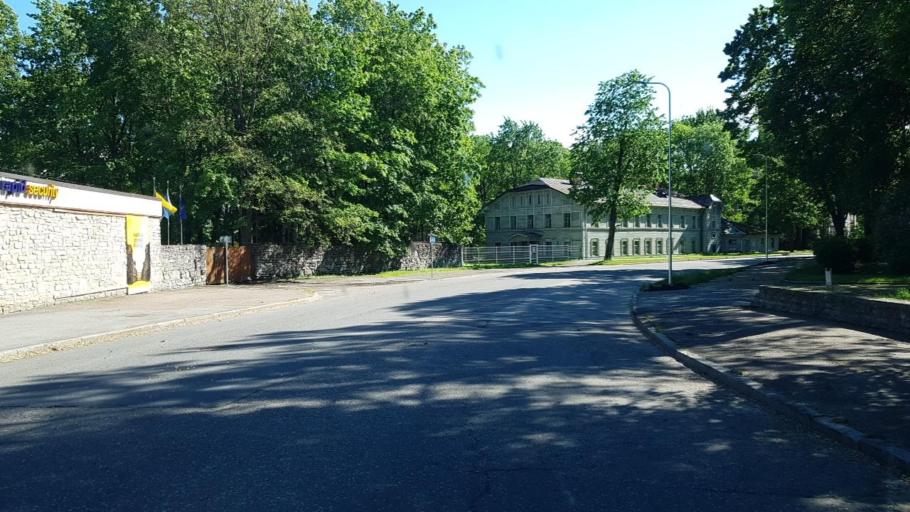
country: EE
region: Ida-Virumaa
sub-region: Narva linn
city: Narva
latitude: 59.3612
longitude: 28.1952
